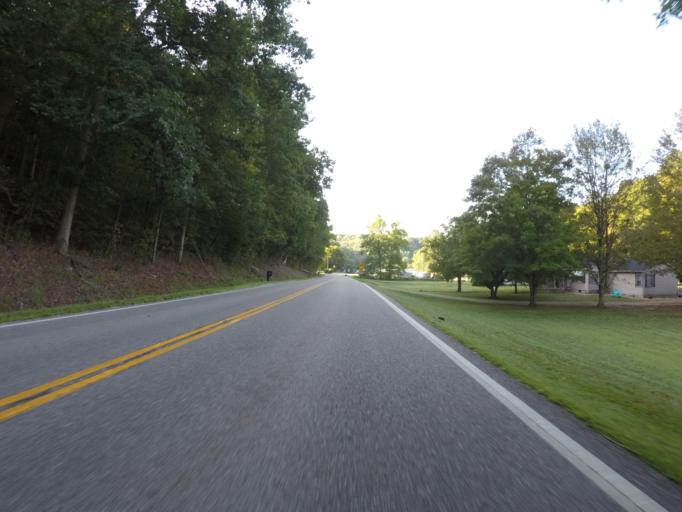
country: US
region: Ohio
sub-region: Lawrence County
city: Coal Grove
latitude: 38.5675
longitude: -82.5517
